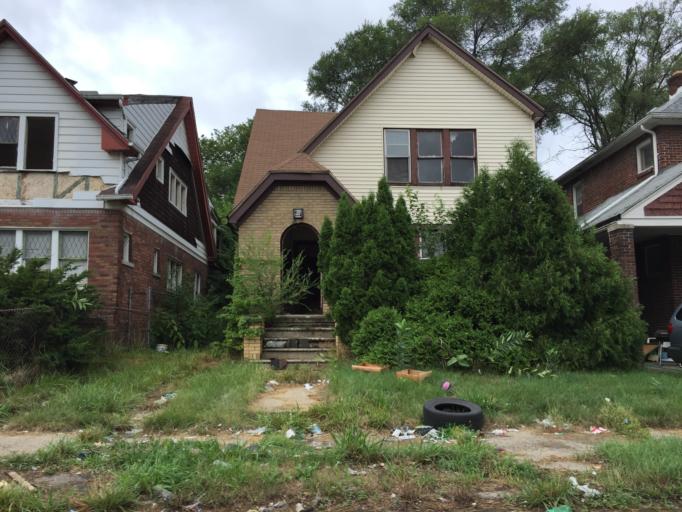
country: US
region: Michigan
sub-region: Oakland County
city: Ferndale
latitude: 42.4069
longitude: -83.1555
